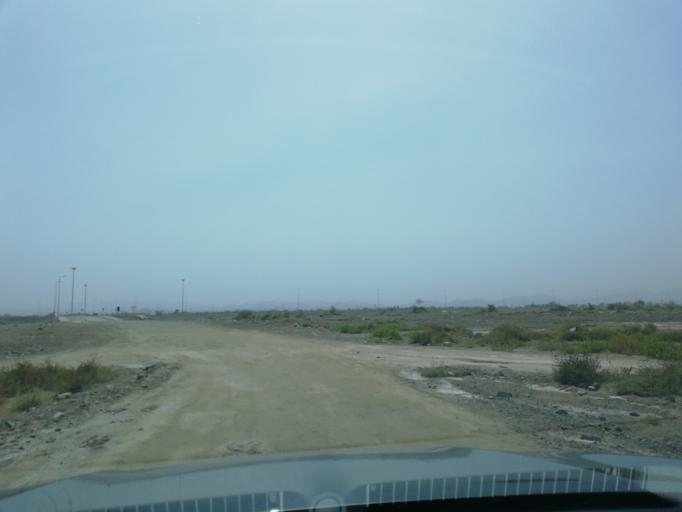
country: OM
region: Al Batinah
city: Shinas
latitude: 24.8651
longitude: 56.4156
